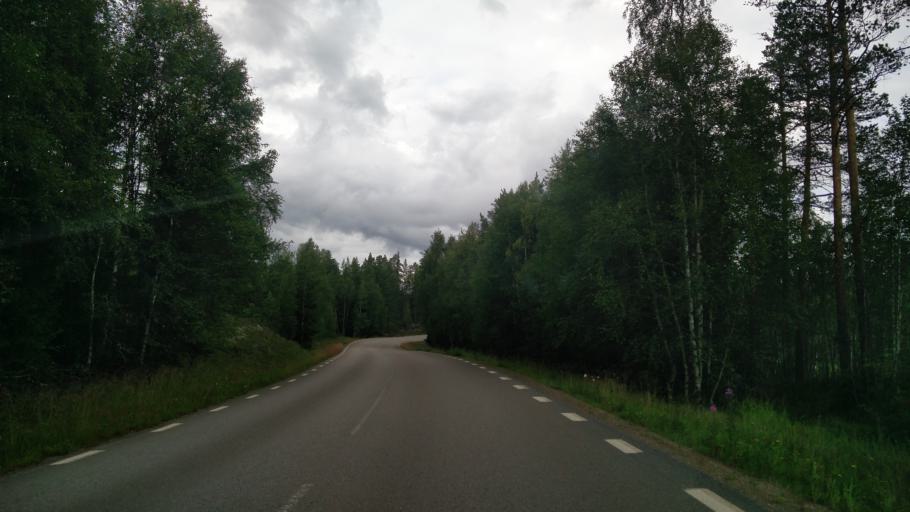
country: NO
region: Hedmark
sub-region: Trysil
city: Innbygda
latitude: 61.1544
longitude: 12.8128
